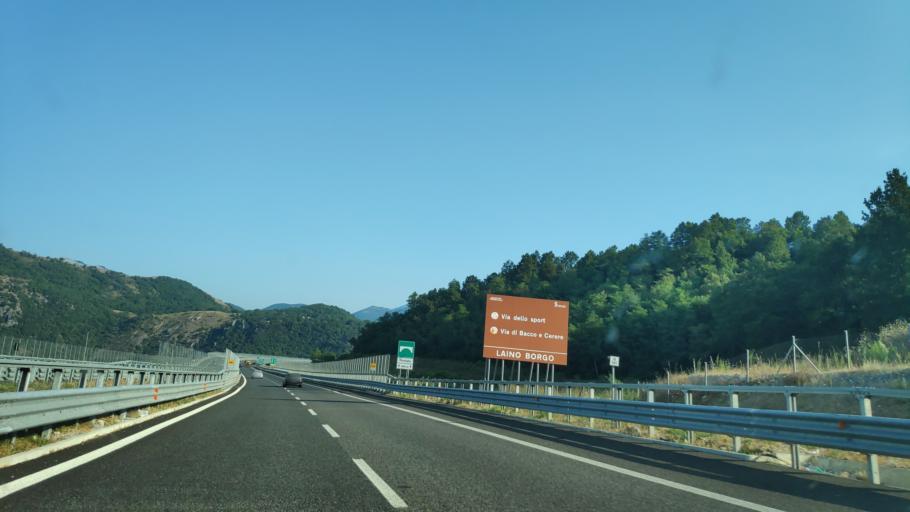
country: IT
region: Calabria
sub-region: Provincia di Cosenza
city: Laino Castello-Nuovo Centro
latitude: 39.9308
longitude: 15.9640
